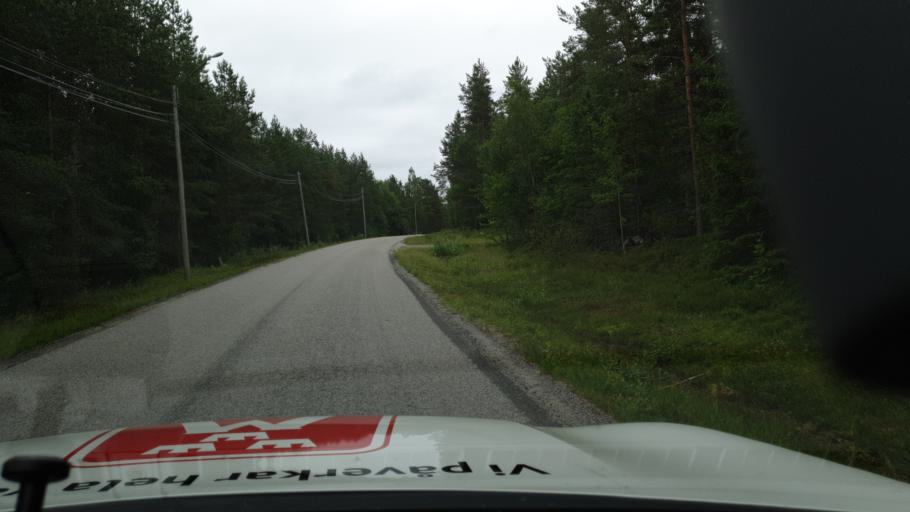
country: SE
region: Vaesterbotten
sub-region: Robertsfors Kommun
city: Robertsfors
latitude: 63.9954
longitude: 20.8166
